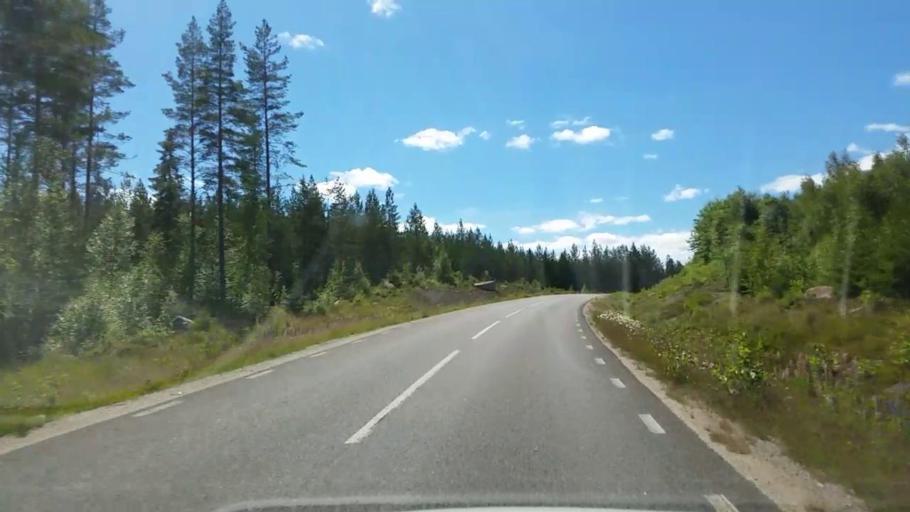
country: SE
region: Gaevleborg
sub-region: Ljusdals Kommun
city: Farila
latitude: 61.6294
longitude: 15.5744
